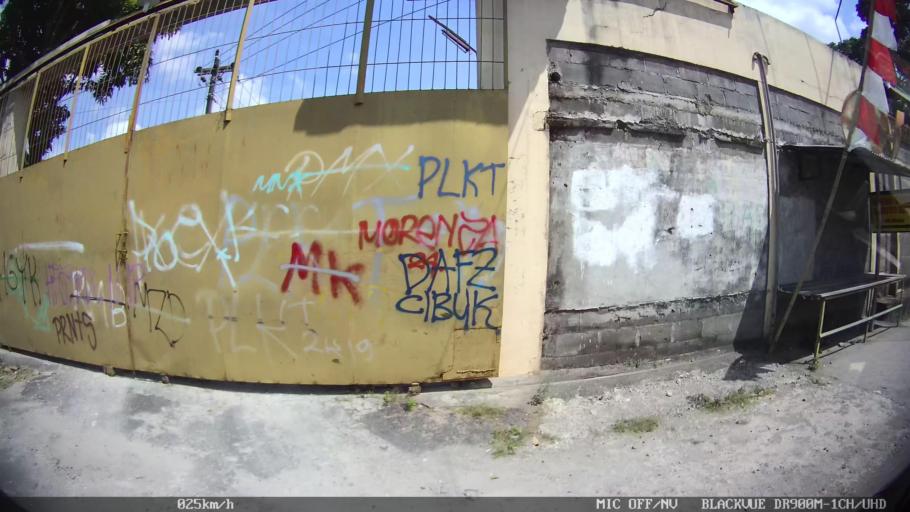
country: ID
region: Daerah Istimewa Yogyakarta
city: Yogyakarta
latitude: -7.8282
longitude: 110.3881
